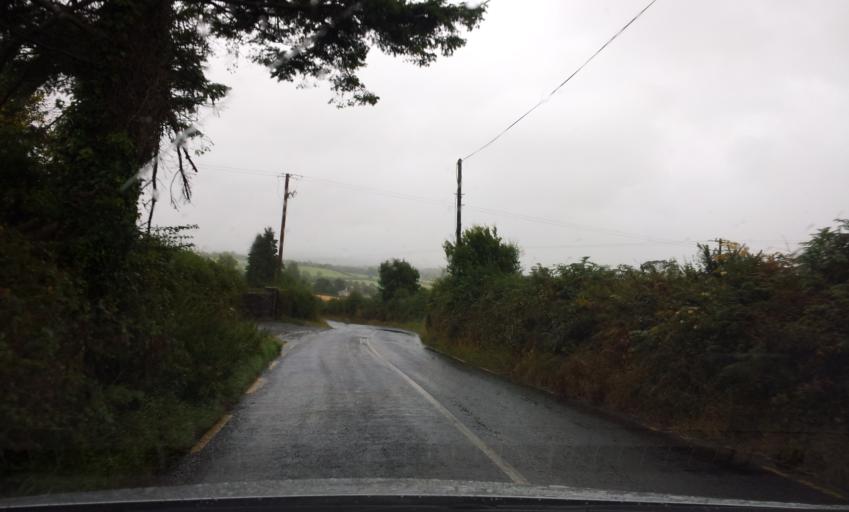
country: IE
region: Leinster
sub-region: Loch Garman
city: New Ross
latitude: 52.4079
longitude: -7.0253
